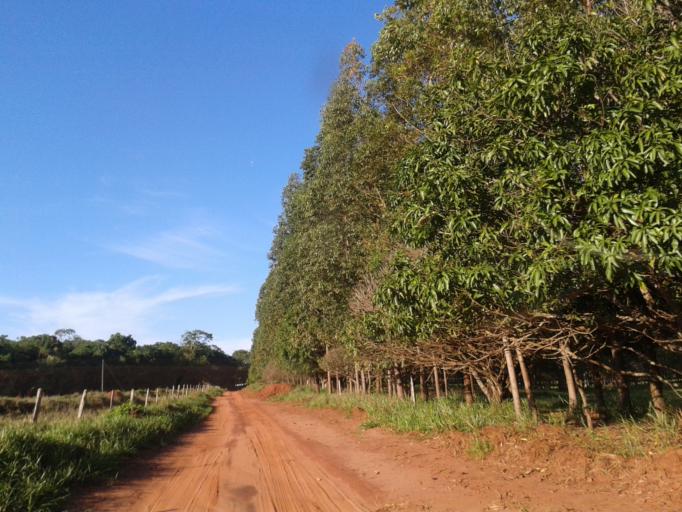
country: BR
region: Minas Gerais
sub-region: Santa Vitoria
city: Santa Vitoria
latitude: -18.9693
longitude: -49.8823
